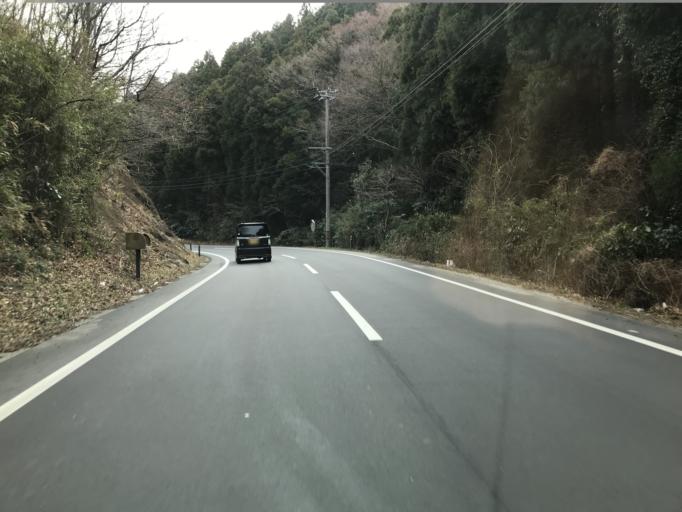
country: JP
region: Fukushima
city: Iwaki
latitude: 37.1073
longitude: 140.8775
